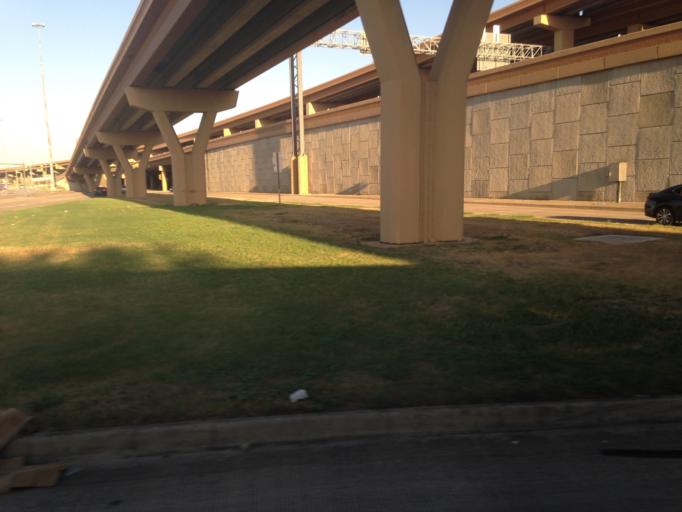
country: US
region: Texas
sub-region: Tarrant County
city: North Richland Hills
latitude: 32.8337
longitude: -97.2027
